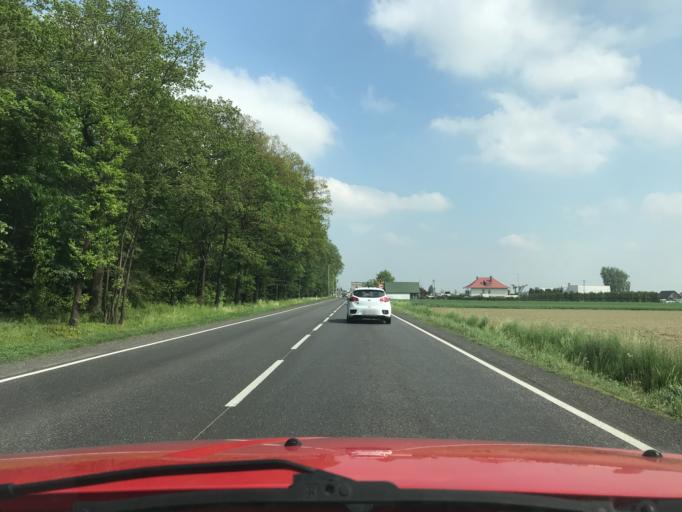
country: PL
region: Greater Poland Voivodeship
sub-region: Powiat pleszewski
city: Czermin
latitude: 51.9068
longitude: 17.7316
